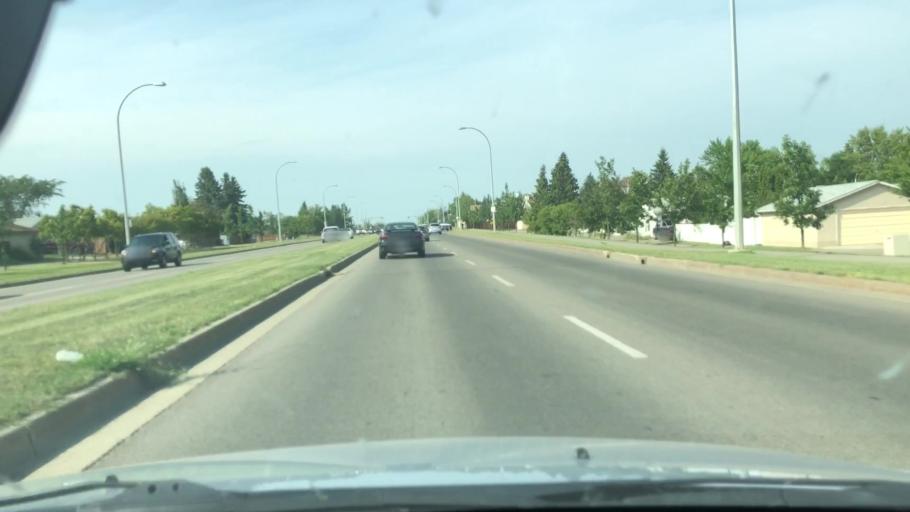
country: CA
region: Alberta
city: Edmonton
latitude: 53.6122
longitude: -113.4428
